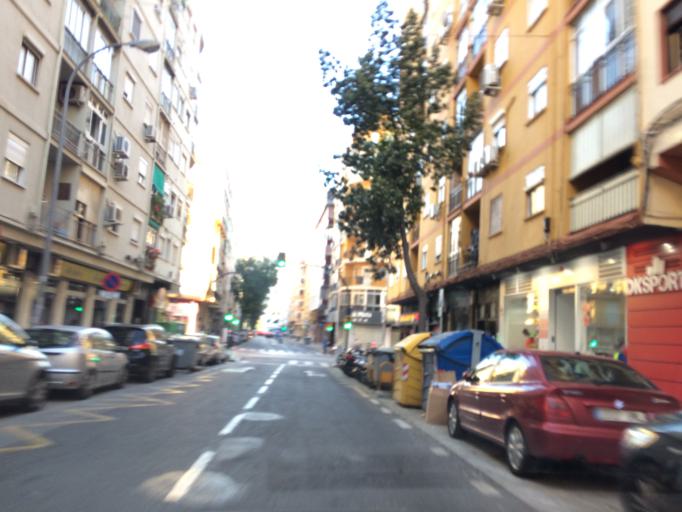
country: ES
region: Andalusia
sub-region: Provincia de Malaga
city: Malaga
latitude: 36.7220
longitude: -4.4326
